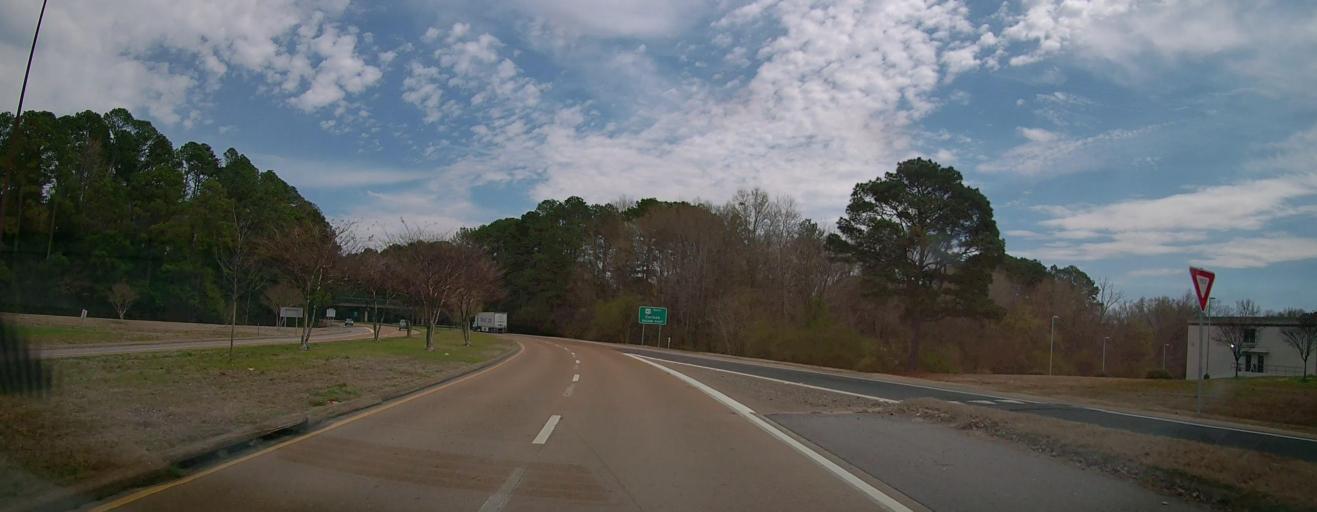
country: US
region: Mississippi
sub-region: Lee County
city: Tupelo
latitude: 34.2725
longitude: -88.7139
